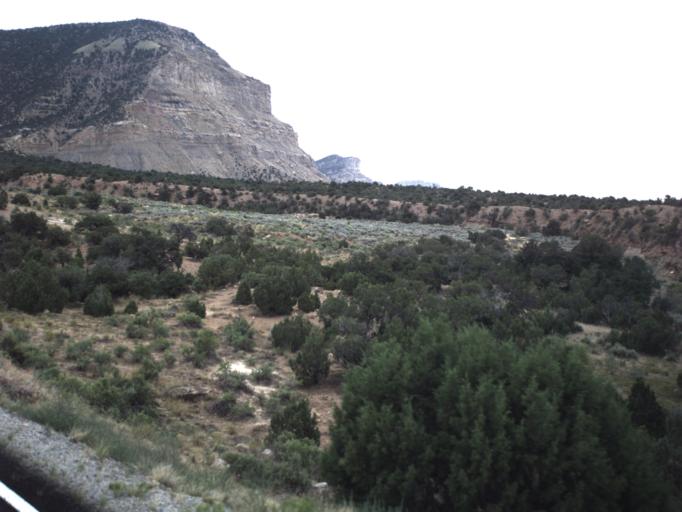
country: US
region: Utah
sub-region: Carbon County
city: East Carbon City
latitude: 39.4529
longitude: -110.3781
